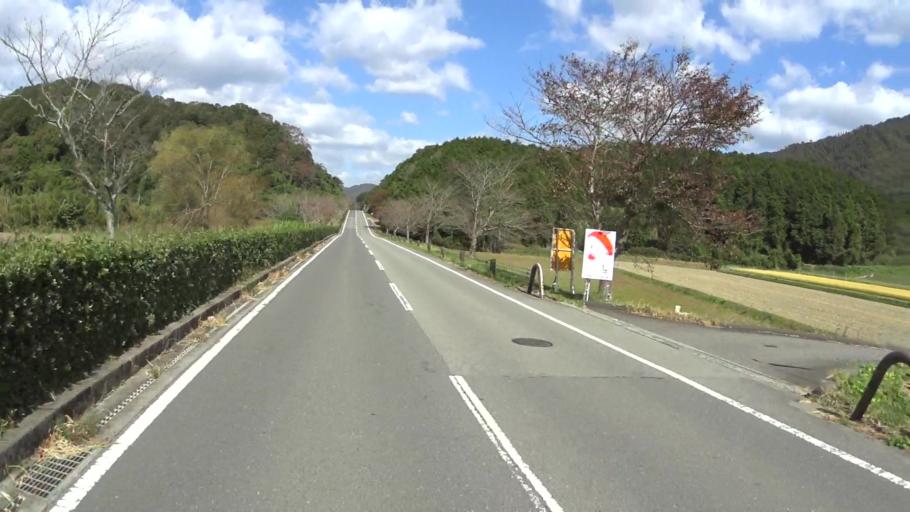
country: JP
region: Kyoto
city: Kameoka
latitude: 35.0677
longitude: 135.5672
